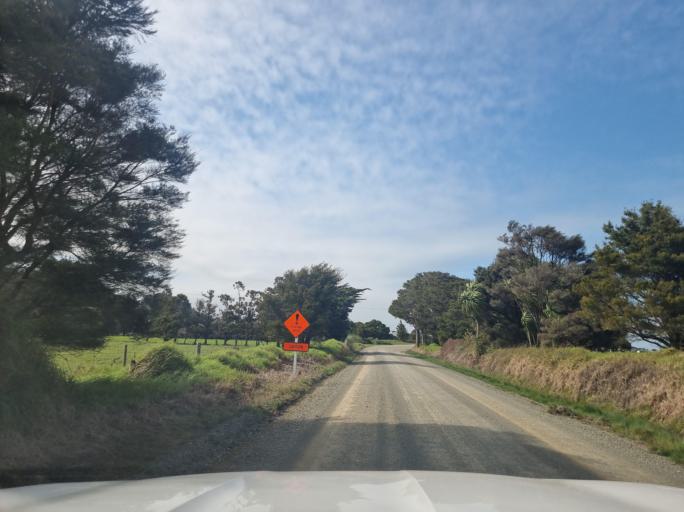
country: NZ
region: Auckland
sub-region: Auckland
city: Wellsford
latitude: -36.1059
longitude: 174.5004
